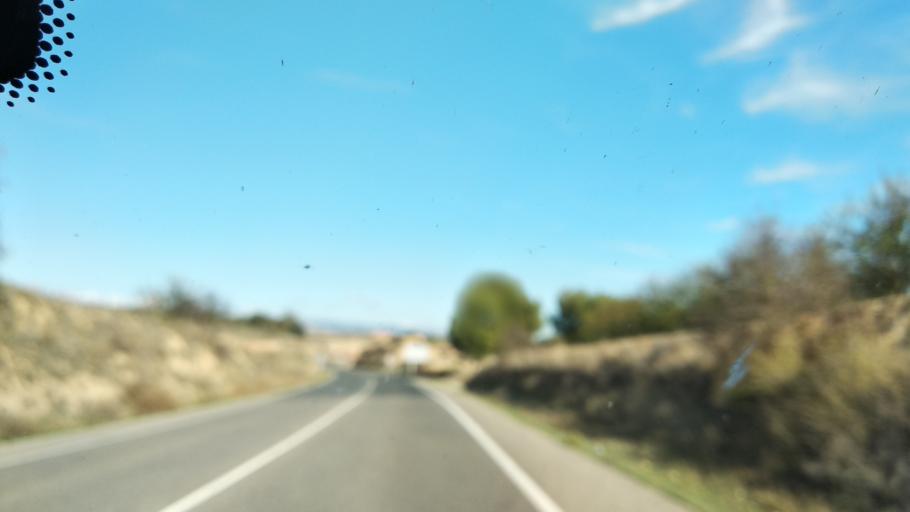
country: ES
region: Catalonia
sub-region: Provincia de Lleida
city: Termens
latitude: 41.7264
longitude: 0.7323
